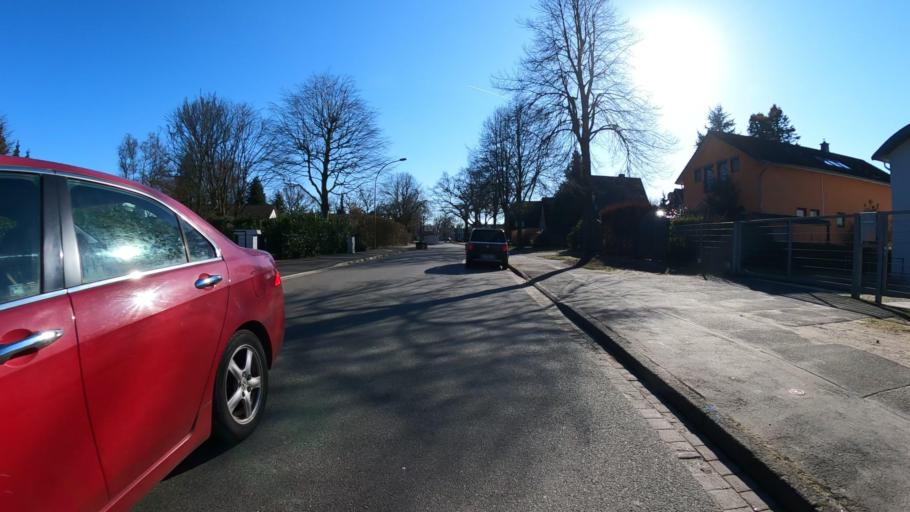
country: DE
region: Schleswig-Holstein
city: Rellingen
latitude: 53.6461
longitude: 9.7972
